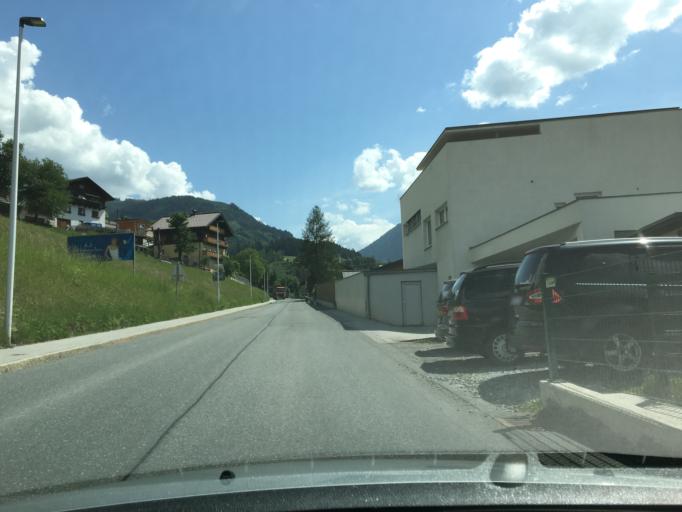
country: AT
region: Salzburg
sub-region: Politischer Bezirk Sankt Johann im Pongau
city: Sankt Johann im Pongau
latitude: 47.3482
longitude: 13.2064
